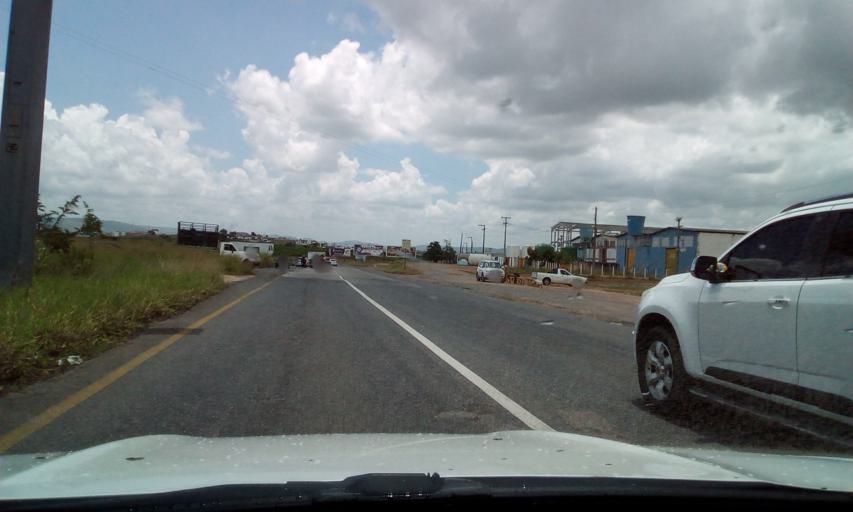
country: BR
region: Pernambuco
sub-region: Vitoria De Santo Antao
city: Vitoria de Santo Antao
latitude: -8.1170
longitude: -35.2593
